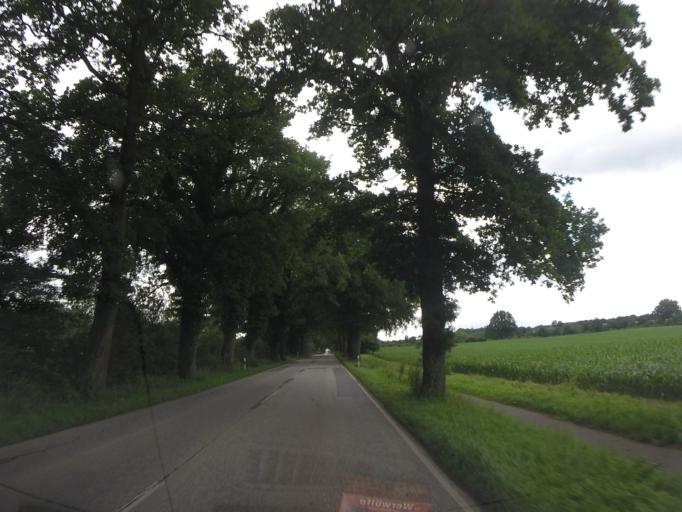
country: DE
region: Schleswig-Holstein
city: Ratekau
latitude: 53.9720
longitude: 10.7174
